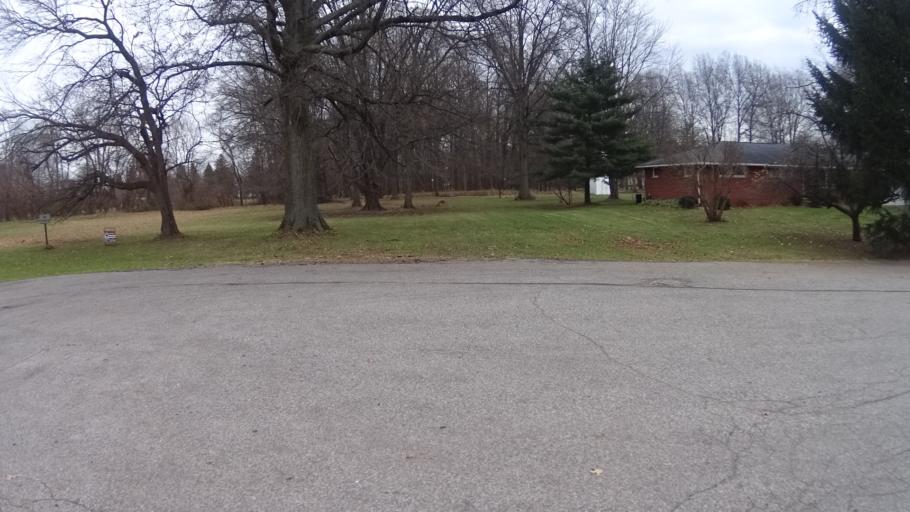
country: US
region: Ohio
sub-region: Lorain County
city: North Ridgeville
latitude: 41.3870
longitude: -82.0227
